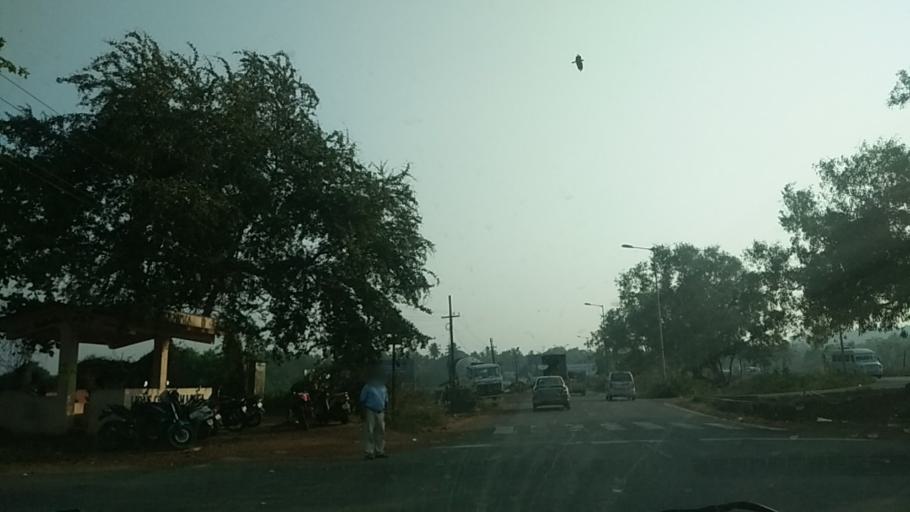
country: IN
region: Goa
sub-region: North Goa
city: Guirim
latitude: 15.5732
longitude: 73.8067
